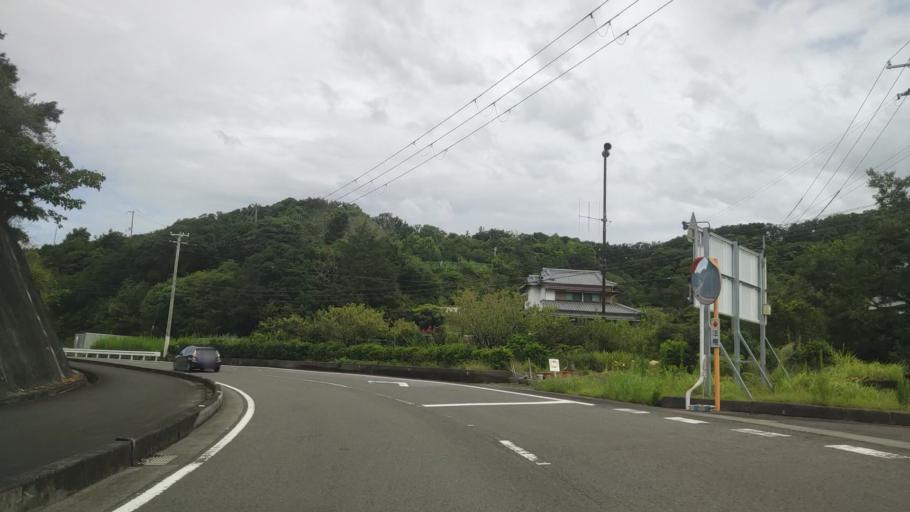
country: JP
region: Wakayama
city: Tanabe
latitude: 33.6825
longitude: 135.3890
